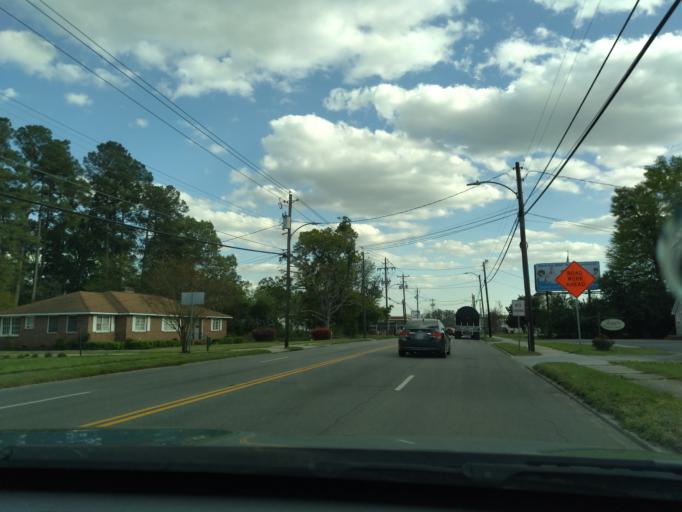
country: US
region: South Carolina
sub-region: Williamsburg County
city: Kingstree
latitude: 33.6687
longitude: -79.8353
